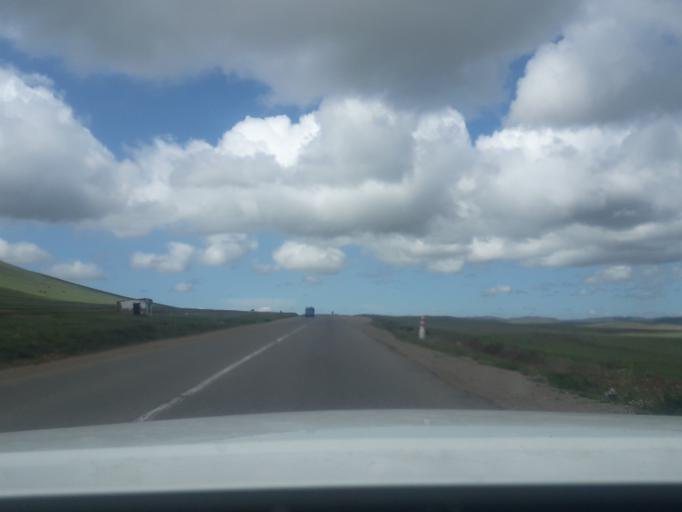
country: MN
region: Central Aimak
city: Altanbulag
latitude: 47.9007
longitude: 106.4165
